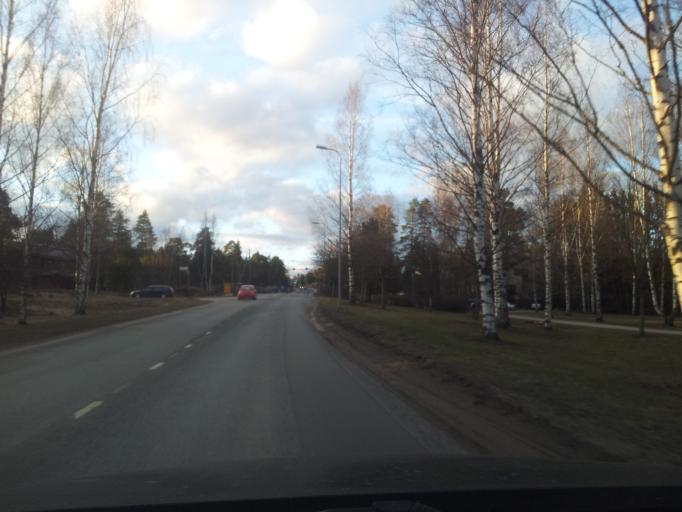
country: FI
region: Uusimaa
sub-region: Helsinki
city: Koukkuniemi
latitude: 60.1714
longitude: 24.7467
